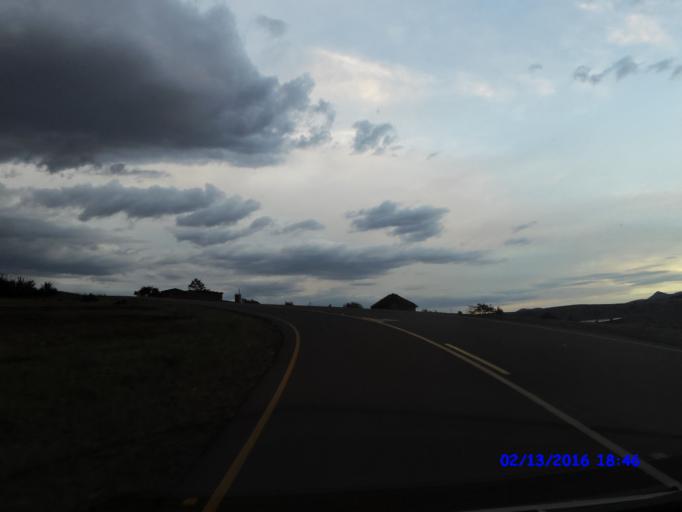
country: LS
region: Qacha's Nek
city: Qacha's Nek
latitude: -30.0557
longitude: 28.2979
